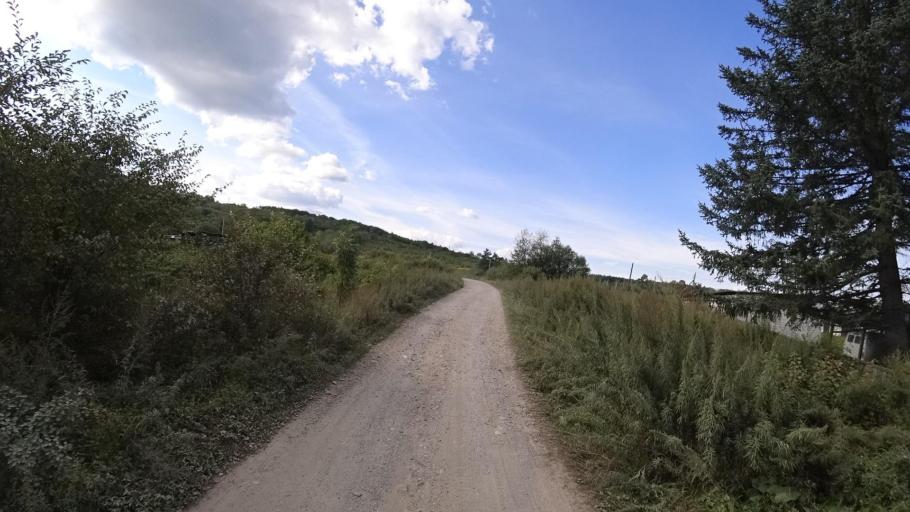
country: RU
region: Jewish Autonomous Oblast
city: Birakan
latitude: 49.0024
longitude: 131.7379
